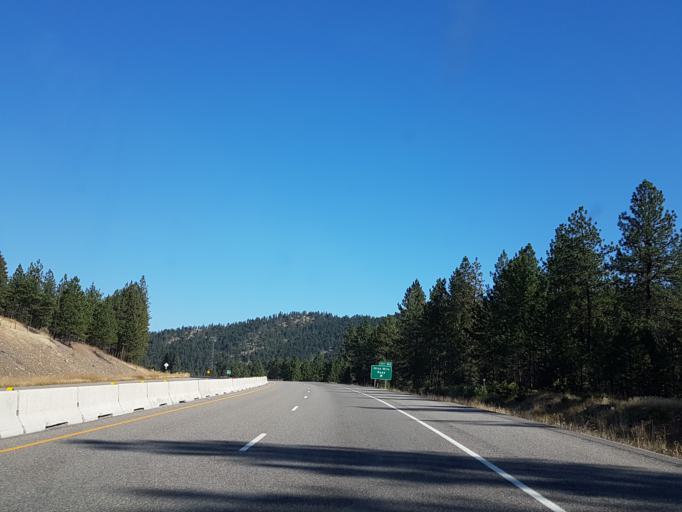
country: US
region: Montana
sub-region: Missoula County
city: Frenchtown
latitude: 47.0192
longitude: -114.3751
